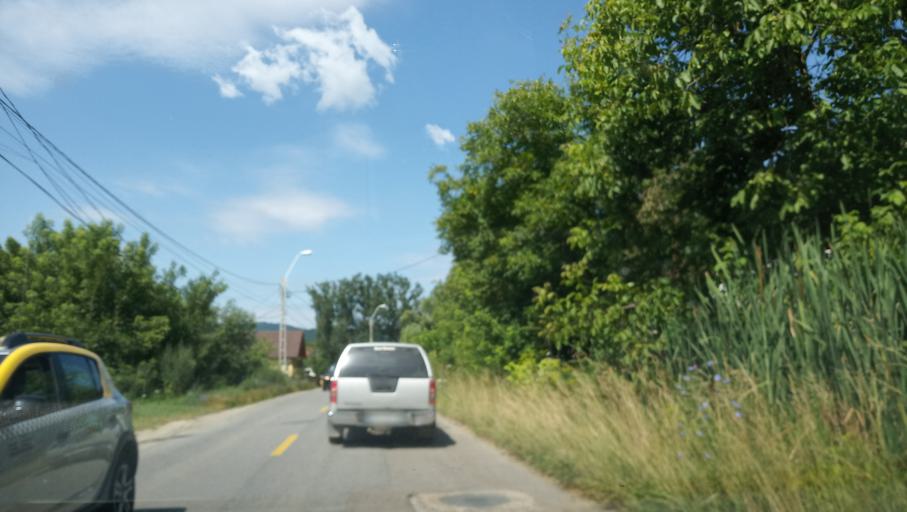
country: RO
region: Hunedoara
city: Hunedoara
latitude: 45.7357
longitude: 22.9125
